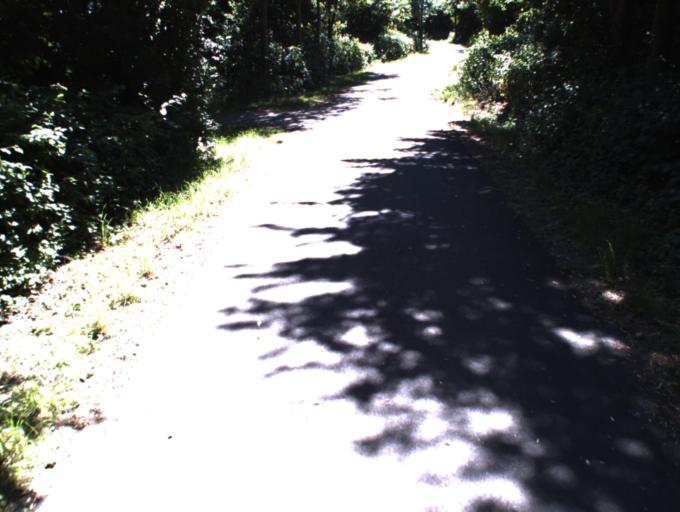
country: SE
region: Skane
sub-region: Helsingborg
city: Rydeback
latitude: 56.0122
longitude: 12.7634
